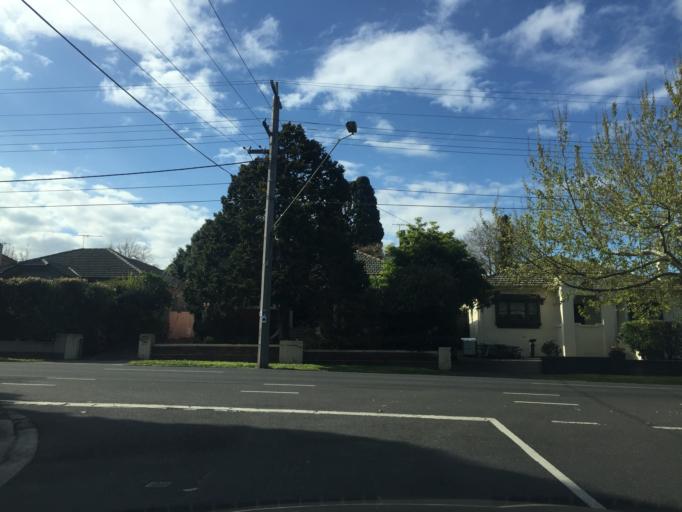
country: AU
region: Victoria
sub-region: Glen Eira
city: Caulfield North
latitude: -37.8648
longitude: 145.0172
